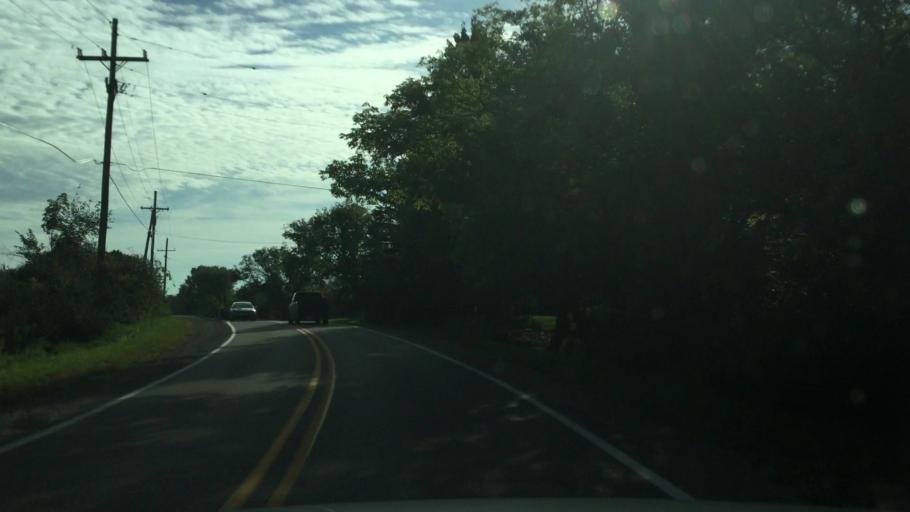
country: US
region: Michigan
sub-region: Livingston County
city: Howell
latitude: 42.6006
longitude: -83.8874
